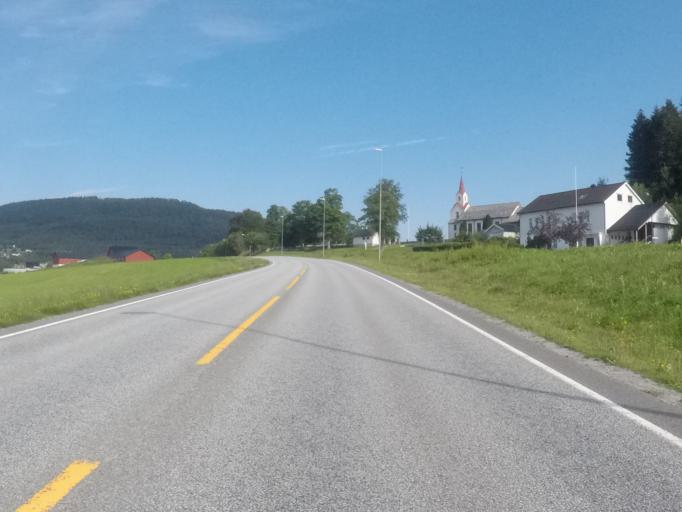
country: NO
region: More og Romsdal
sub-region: Vestnes
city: Vestnes
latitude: 62.6258
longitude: 7.0856
